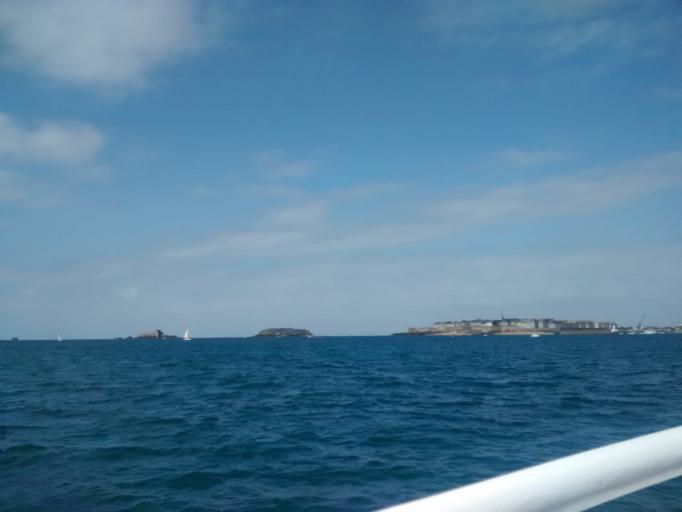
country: FR
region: Brittany
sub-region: Departement d'Ille-et-Vilaine
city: Dinard
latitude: 48.6357
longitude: -2.0427
